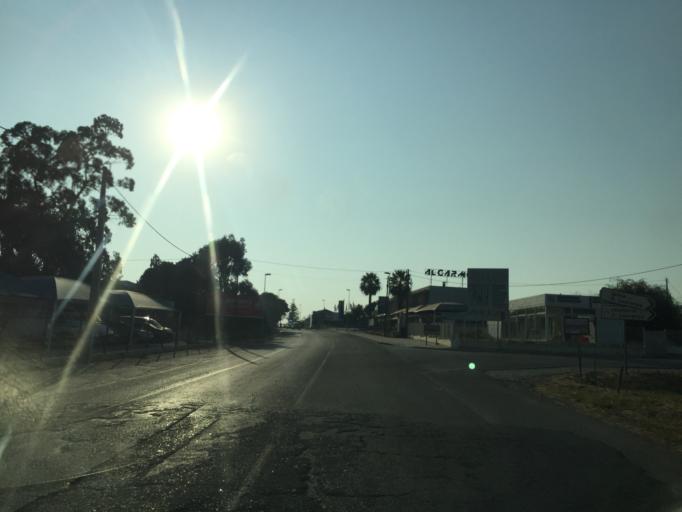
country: PT
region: Faro
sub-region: Loule
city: Almancil
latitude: 37.0839
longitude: -8.0166
